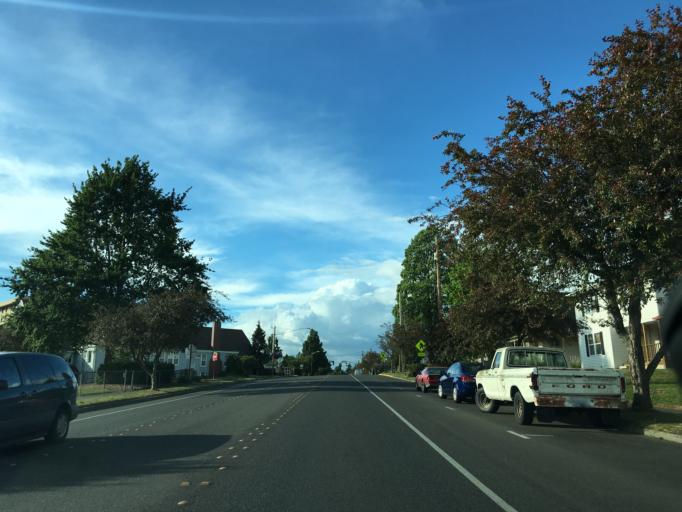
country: US
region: Washington
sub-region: Whatcom County
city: Bellingham
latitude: 48.7607
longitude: -122.4751
